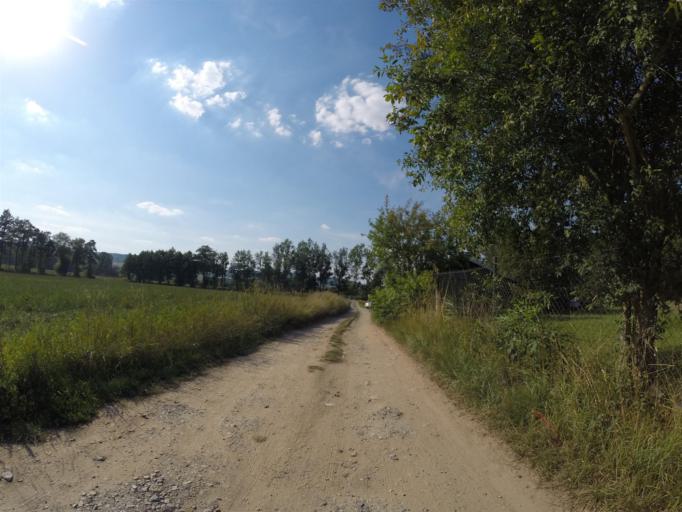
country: DE
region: Thuringia
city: Sulza
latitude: 50.8504
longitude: 11.6205
